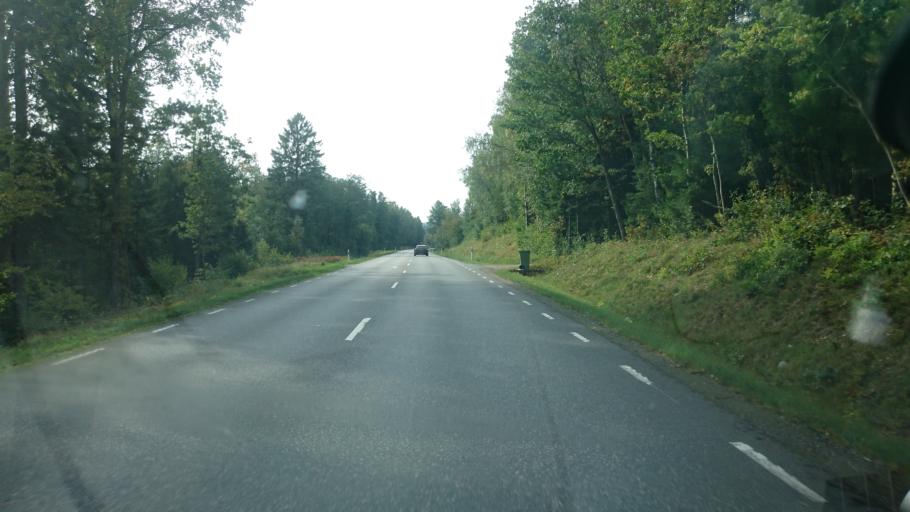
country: SE
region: Vaestra Goetaland
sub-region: Alingsas Kommun
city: Alingsas
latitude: 58.0192
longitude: 12.4548
